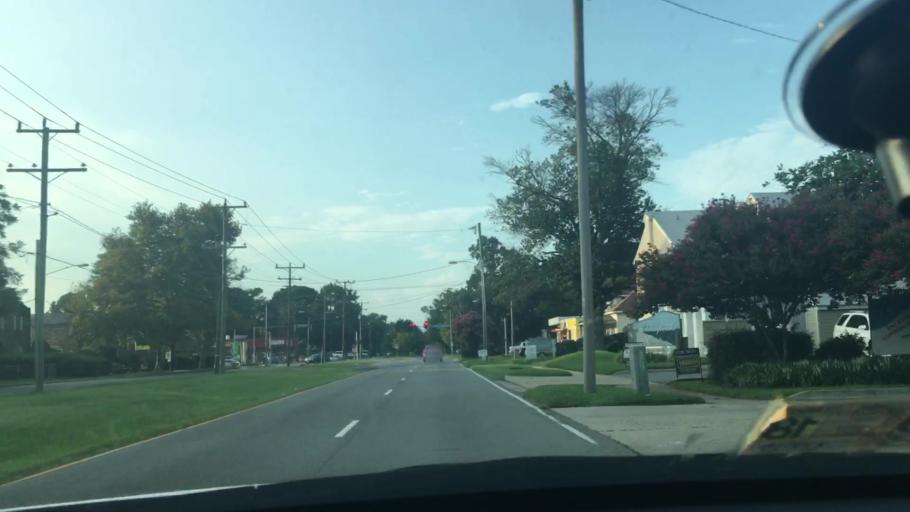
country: US
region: Virginia
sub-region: City of Norfolk
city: Norfolk
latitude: 36.9325
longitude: -76.2441
